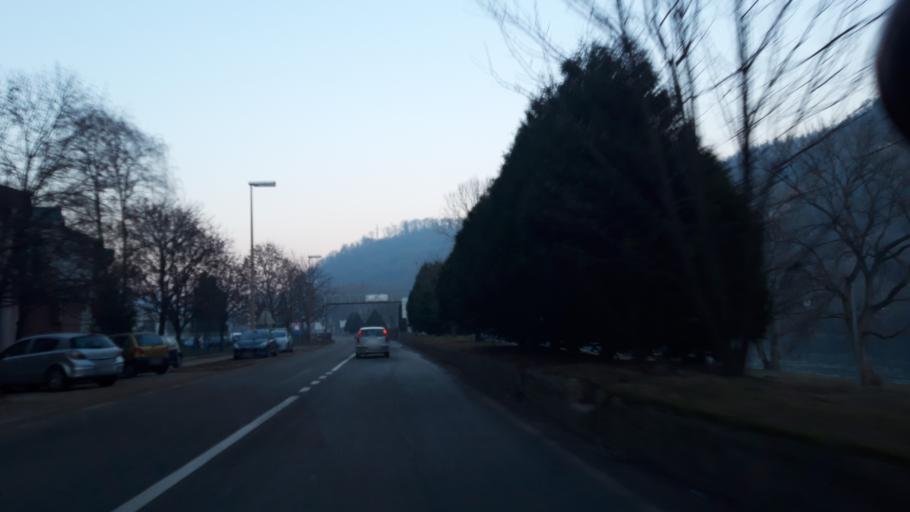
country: BA
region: Republika Srpska
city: Zvornik
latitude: 44.3805
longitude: 19.1039
